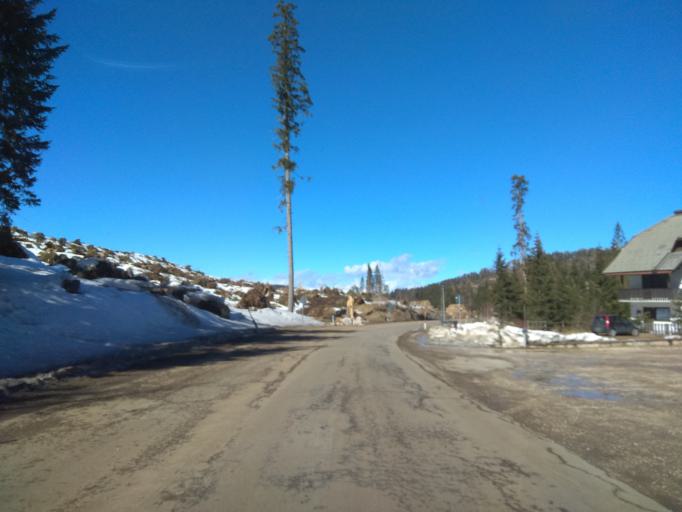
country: IT
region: Trentino-Alto Adige
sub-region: Bolzano
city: Nova Levante
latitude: 46.4082
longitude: 11.5823
